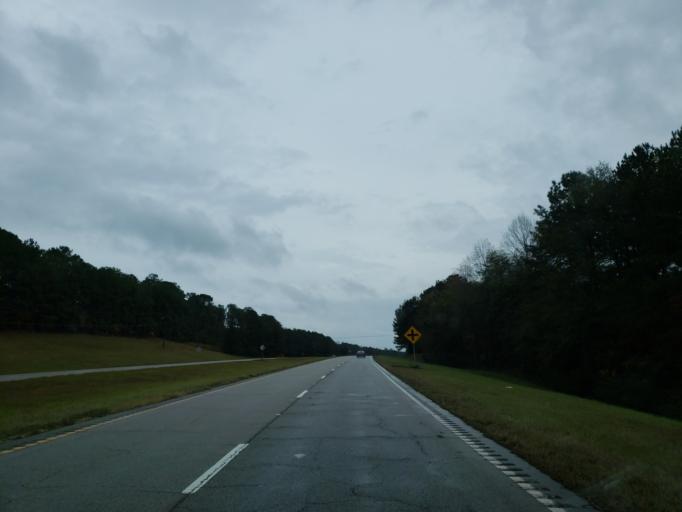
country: US
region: Mississippi
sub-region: Jones County
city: Laurel
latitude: 31.7059
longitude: -89.0651
